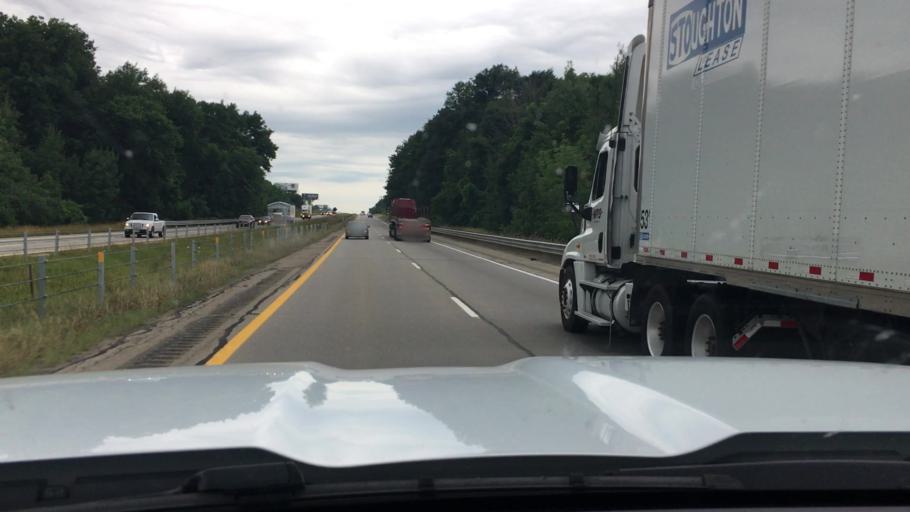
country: US
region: Michigan
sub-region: Kent County
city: Byron Center
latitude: 42.7764
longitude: -85.6699
